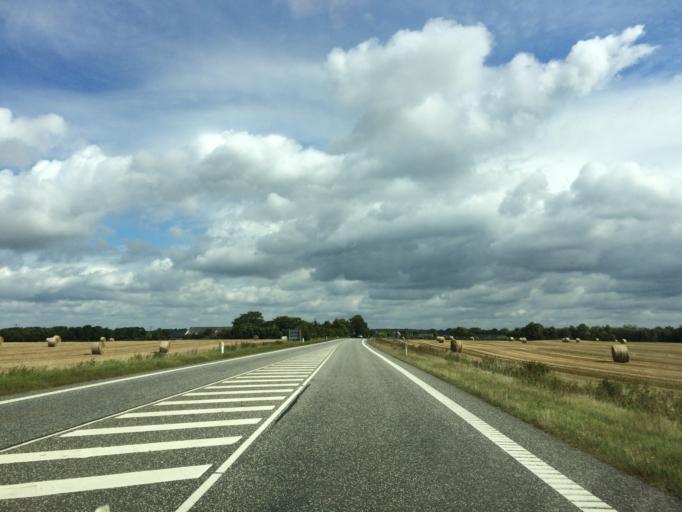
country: DK
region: Central Jutland
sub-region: Holstebro Kommune
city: Vinderup
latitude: 56.3876
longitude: 8.7918
